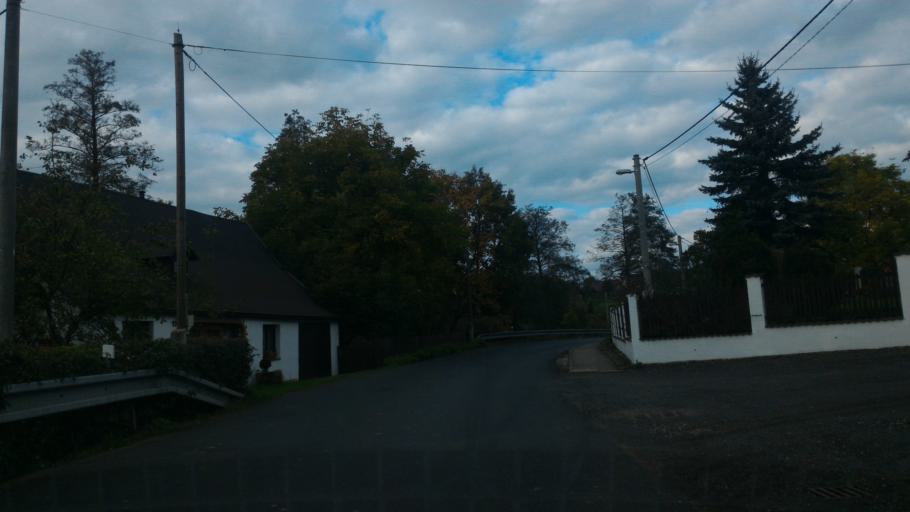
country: CZ
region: Ustecky
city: Benesov nad Ploucnici
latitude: 50.7649
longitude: 14.3419
